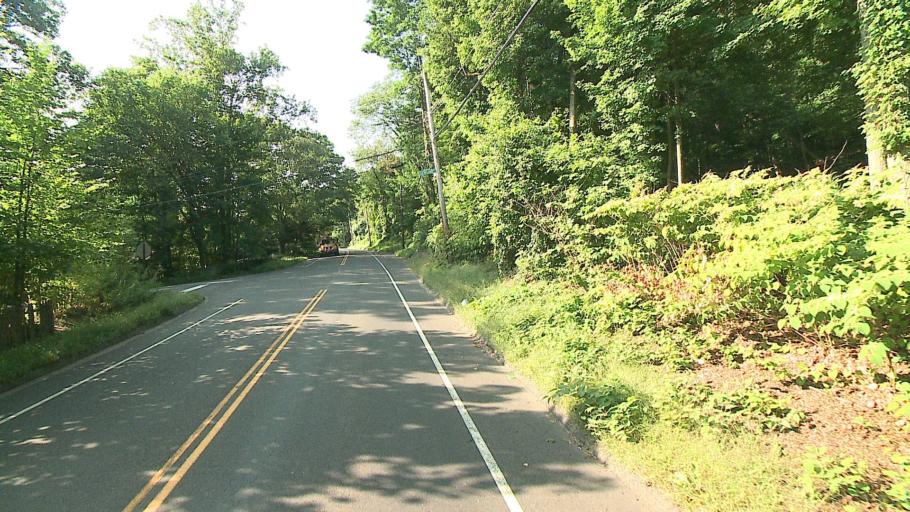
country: US
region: Connecticut
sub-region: New Haven County
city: New Haven
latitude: 41.3158
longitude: -72.9709
